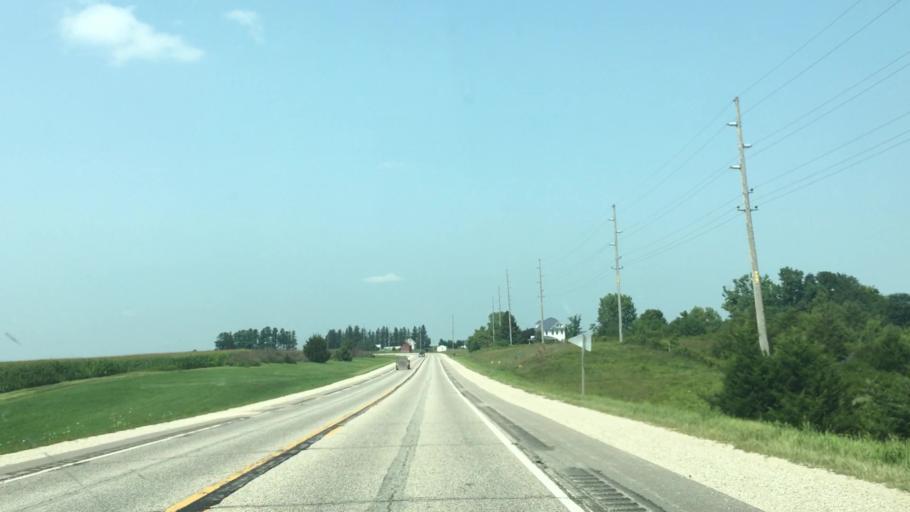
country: US
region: Iowa
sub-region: Fayette County
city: Fayette
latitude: 42.9000
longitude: -91.8103
